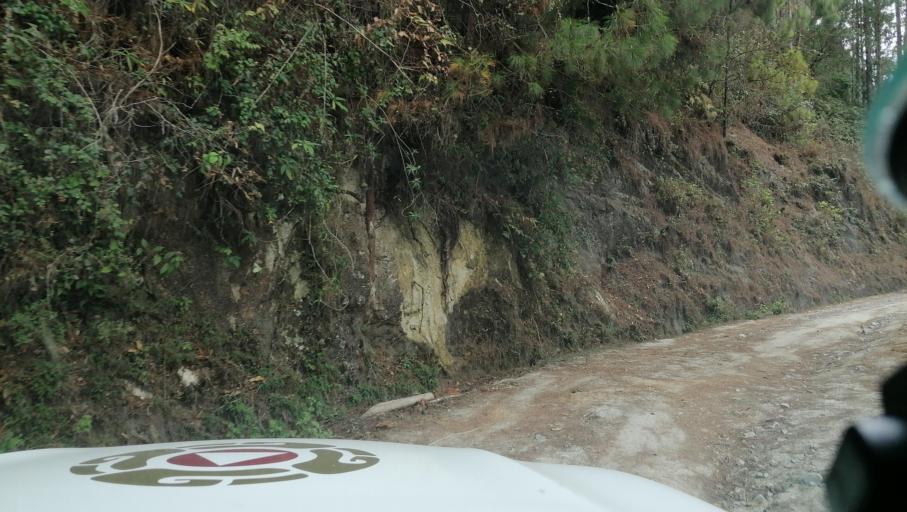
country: MX
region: Chiapas
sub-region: Tapachula
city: Canton Villaflor
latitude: 15.1974
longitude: -92.2329
